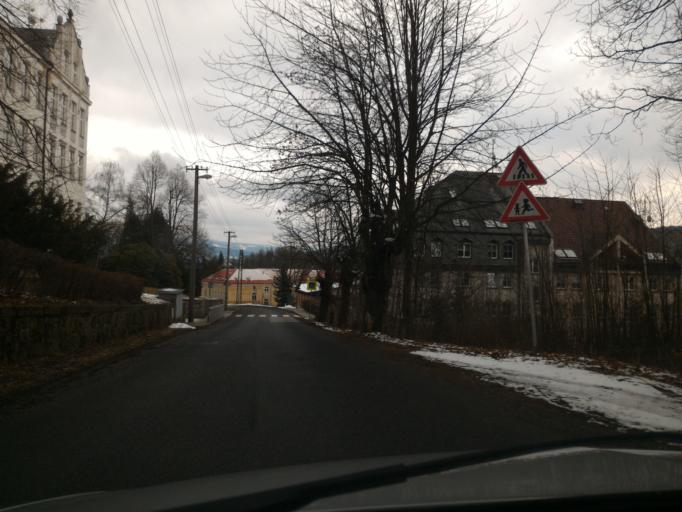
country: CZ
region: Liberecky
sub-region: Okres Jablonec nad Nisou
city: Smrzovka
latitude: 50.7324
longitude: 15.2460
